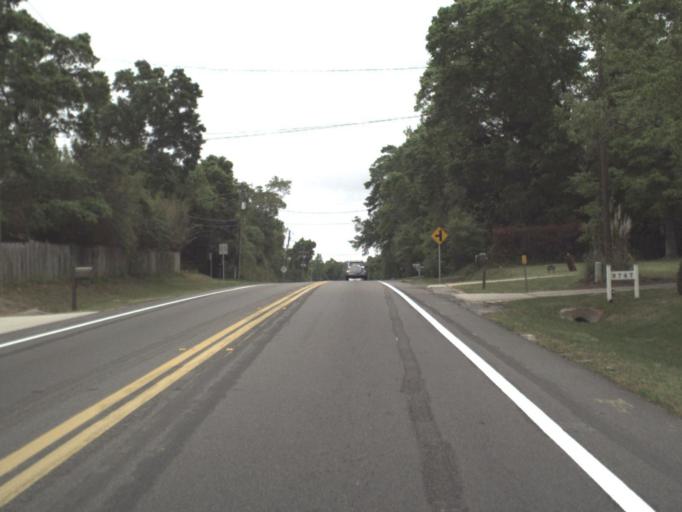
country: US
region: Florida
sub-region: Escambia County
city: Ferry Pass
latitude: 30.5360
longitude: -87.1928
